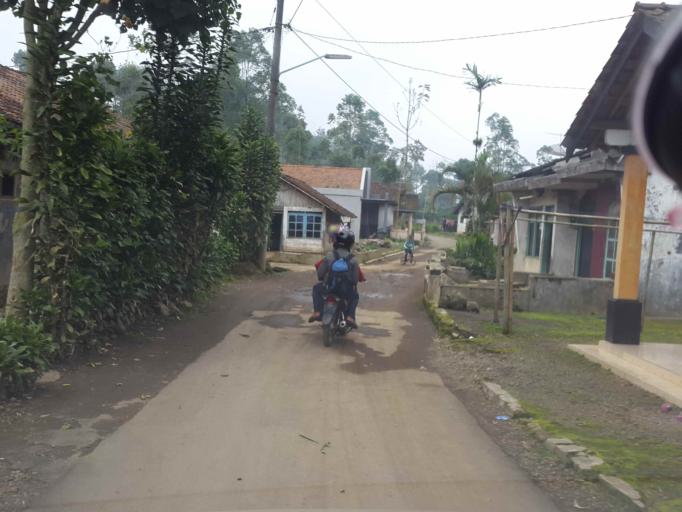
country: ID
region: Central Java
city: Baturaden
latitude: -7.2538
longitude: 109.0801
